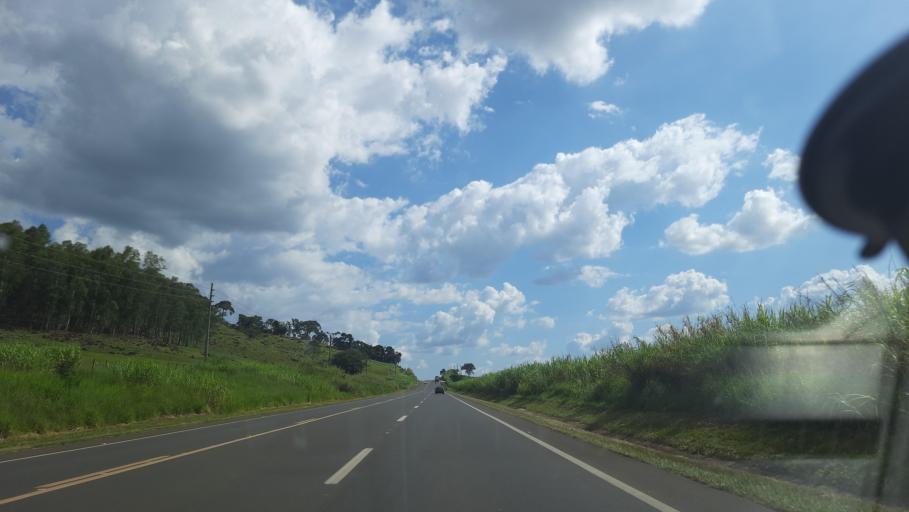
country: BR
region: Sao Paulo
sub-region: Sao Jose Do Rio Pardo
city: Sao Jose do Rio Pardo
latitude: -21.6528
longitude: -46.9124
